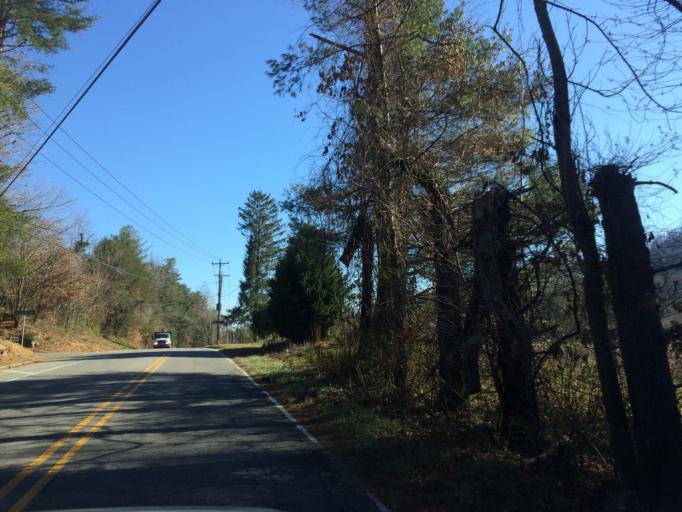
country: US
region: North Carolina
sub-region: Henderson County
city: Laurel Park
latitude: 35.3278
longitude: -82.5079
